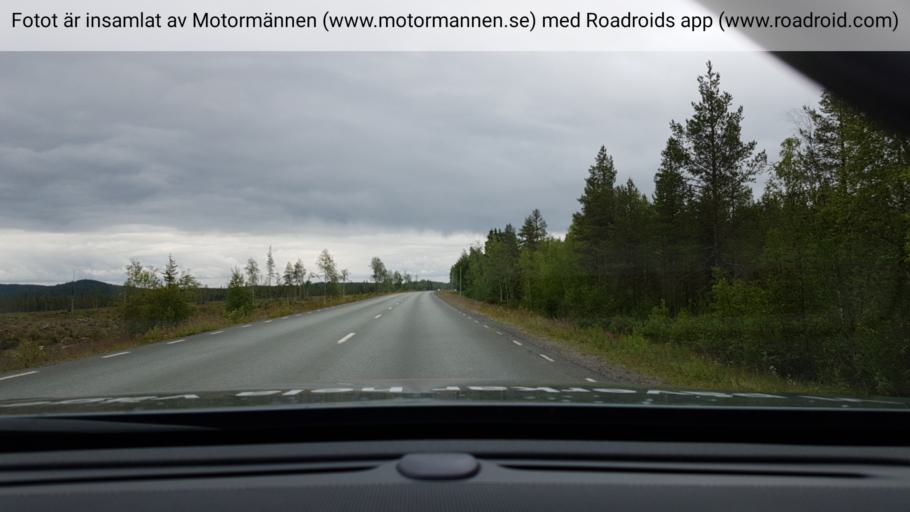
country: SE
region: Vaesterbotten
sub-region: Norsjo Kommun
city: Norsjoe
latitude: 65.2309
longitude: 19.7379
